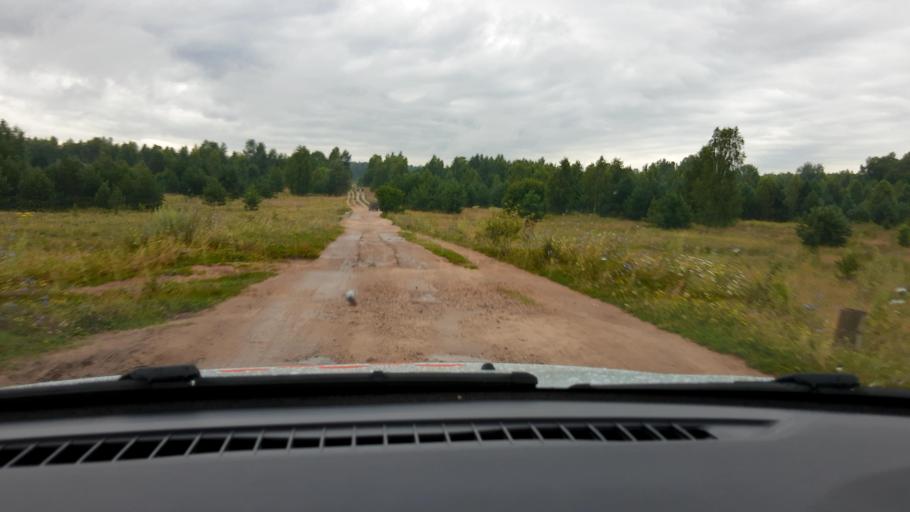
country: RU
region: Nizjnij Novgorod
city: Surovatikha
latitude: 55.9391
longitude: 43.9167
